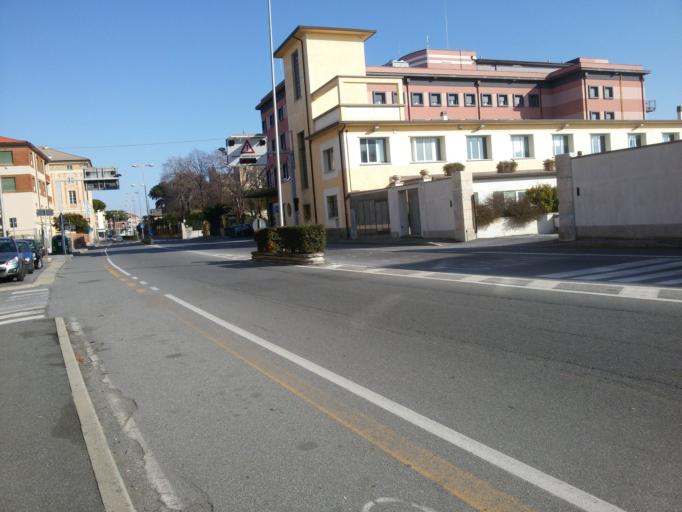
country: IT
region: Liguria
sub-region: Provincia di Savona
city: Valleggia
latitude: 44.2920
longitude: 8.4544
